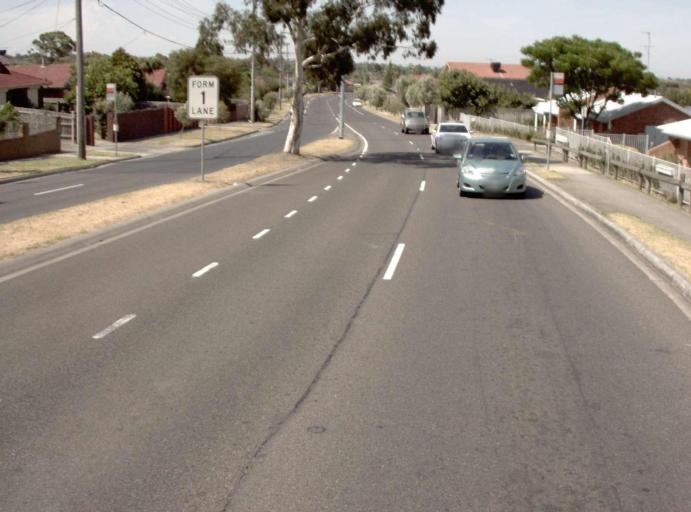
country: AU
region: Victoria
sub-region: Greater Dandenong
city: Noble Park North
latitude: -37.9382
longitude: 145.1923
